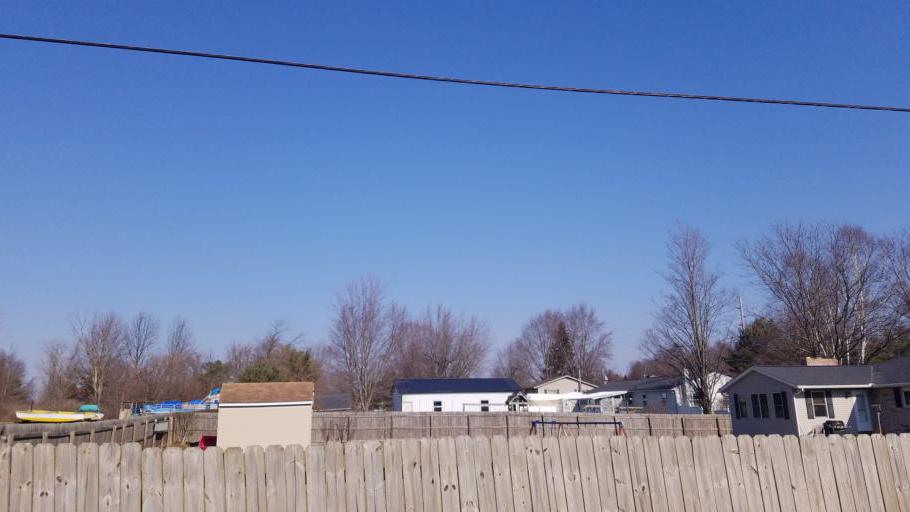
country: US
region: Ohio
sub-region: Crawford County
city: Galion
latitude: 40.7122
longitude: -82.7866
